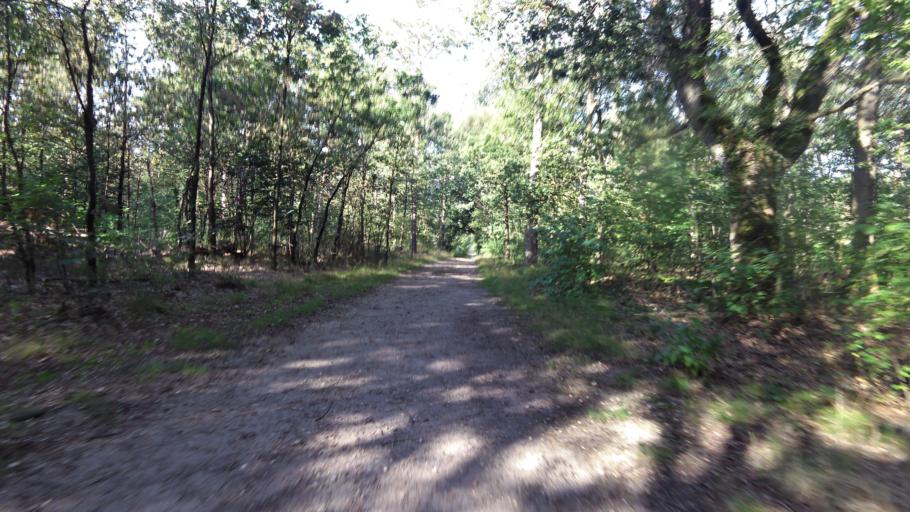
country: NL
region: Gelderland
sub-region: Gemeente Renkum
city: Renkum
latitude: 52.0015
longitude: 5.7245
